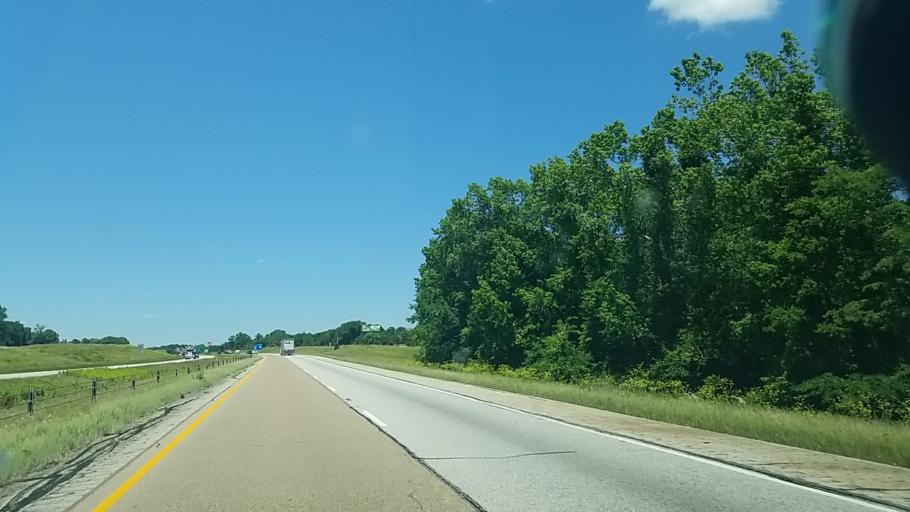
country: US
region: Texas
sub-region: Leon County
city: Centerville
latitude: 31.2452
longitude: -95.9901
